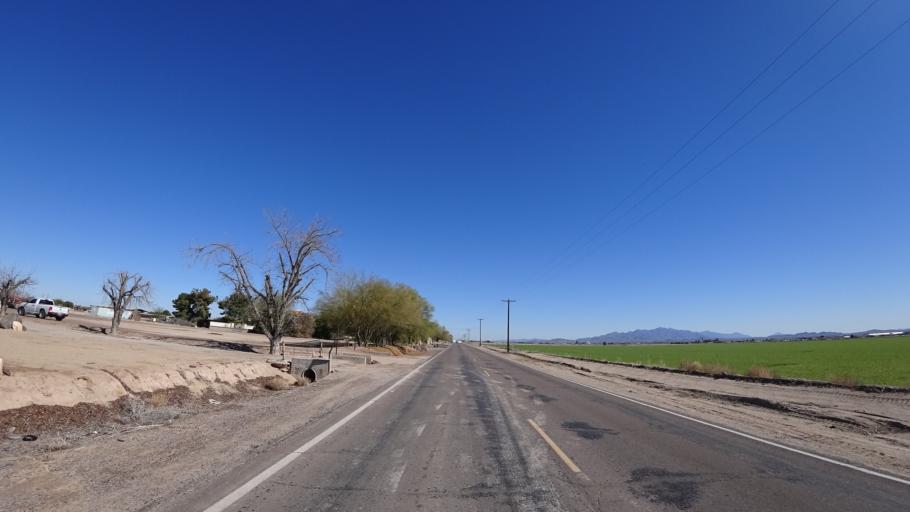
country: US
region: Arizona
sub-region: Maricopa County
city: Buckeye
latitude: 33.4067
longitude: -112.5527
